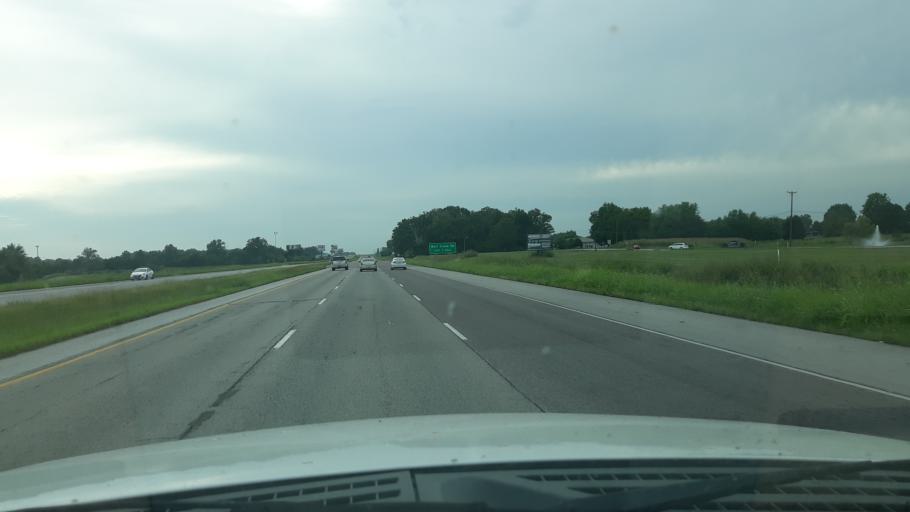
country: US
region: Illinois
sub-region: Williamson County
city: Energy
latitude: 37.7452
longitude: -89.0318
